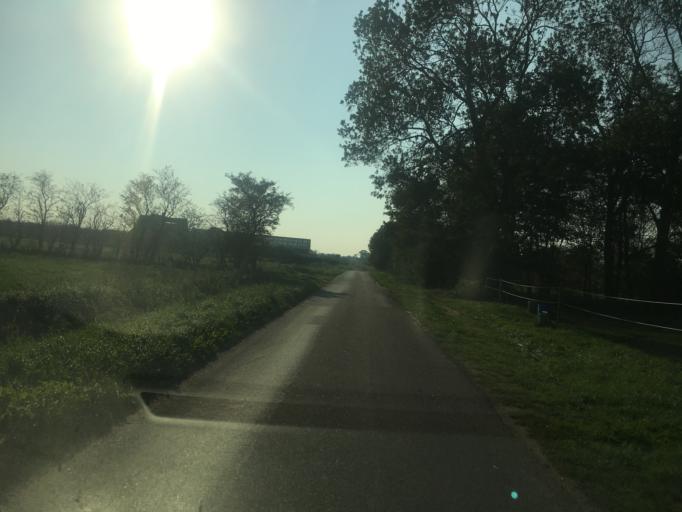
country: DE
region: Schleswig-Holstein
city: Ladelund
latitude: 54.9199
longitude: 9.0389
